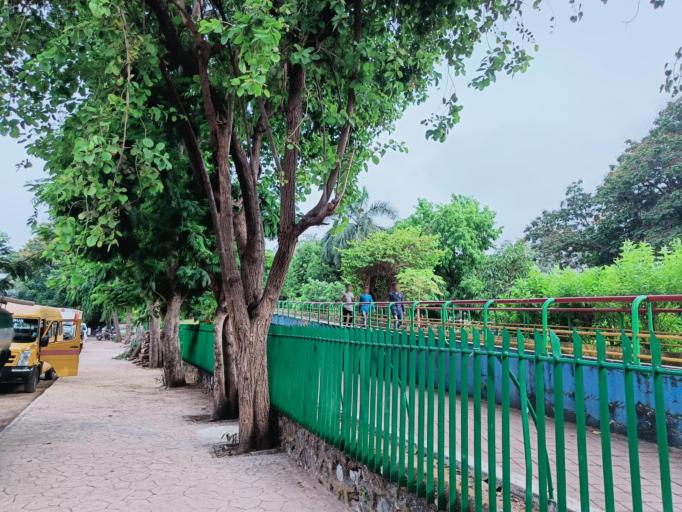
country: IN
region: Maharashtra
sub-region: Mumbai Suburban
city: Mumbai
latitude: 19.1055
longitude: 72.8313
